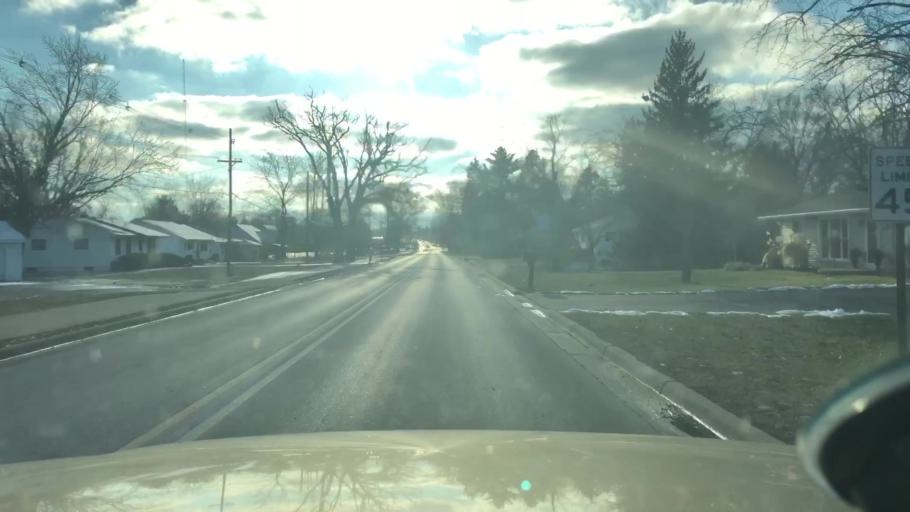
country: US
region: Michigan
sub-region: Jackson County
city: Vandercook Lake
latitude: 42.2076
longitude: -84.4292
